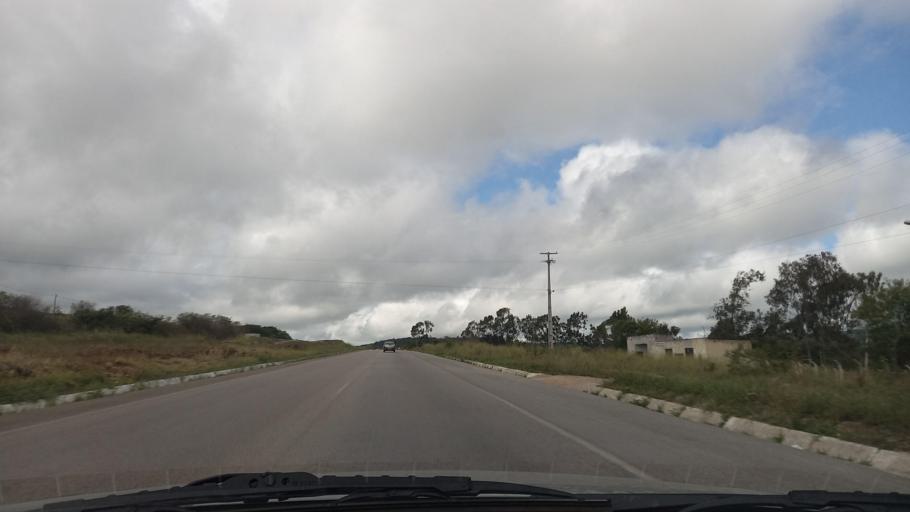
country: BR
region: Pernambuco
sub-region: Caruaru
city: Caruaru
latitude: -8.3178
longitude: -35.9914
